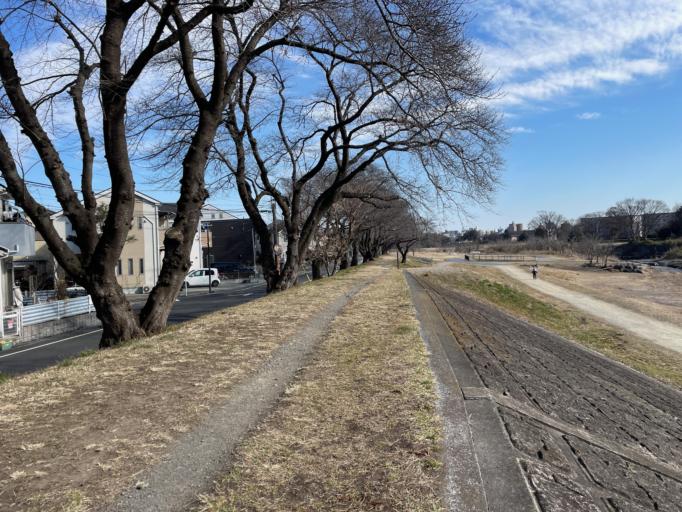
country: JP
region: Tokyo
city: Hachioji
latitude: 35.6711
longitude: 139.3089
